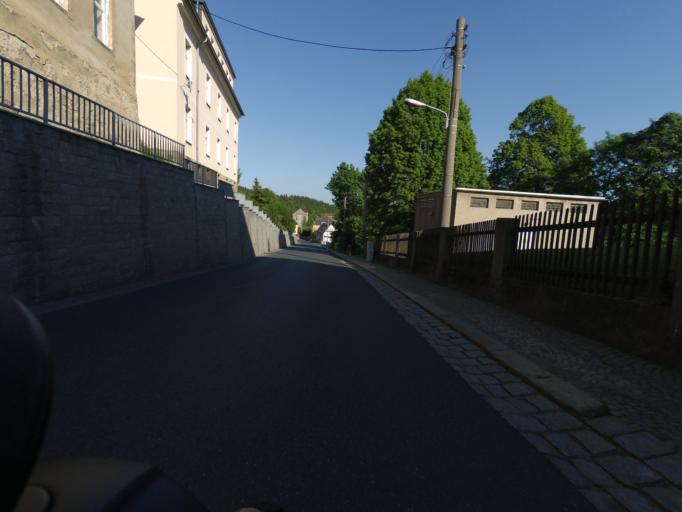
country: DE
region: Saxony
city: Rabenau
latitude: 50.9624
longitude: 13.6417
